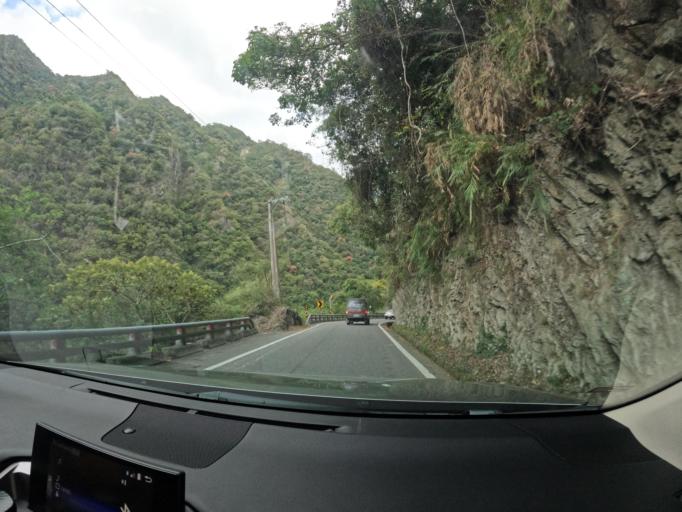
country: TW
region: Taiwan
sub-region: Taitung
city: Taitung
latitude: 23.1415
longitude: 121.1008
